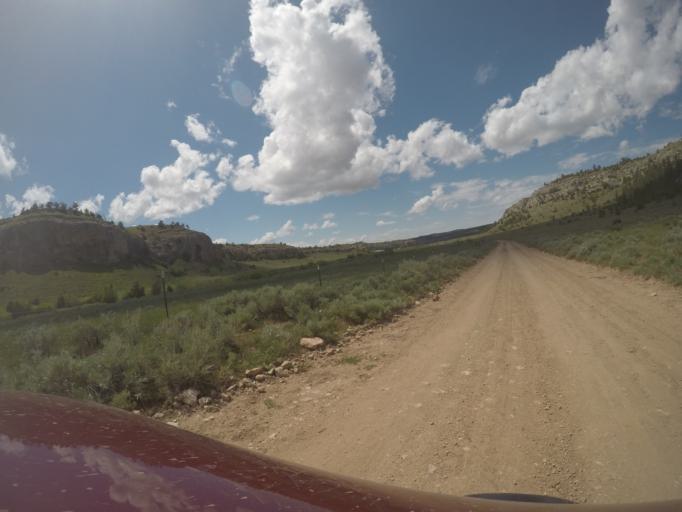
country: US
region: Montana
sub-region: Yellowstone County
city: Laurel
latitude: 45.2361
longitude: -108.6223
